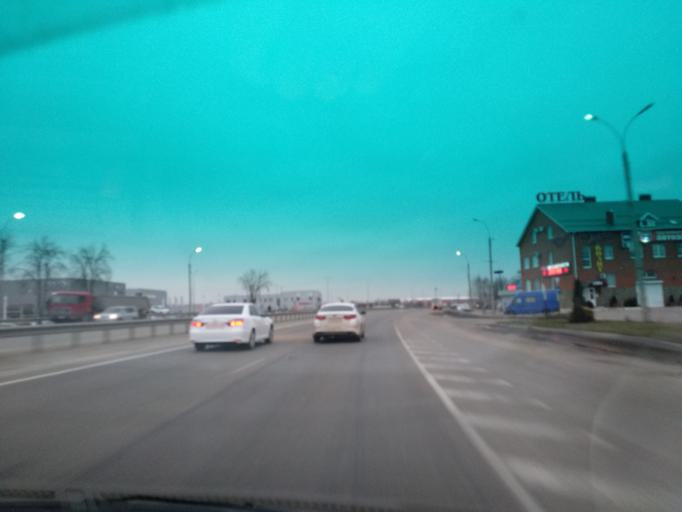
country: RU
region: Krasnodarskiy
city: Pashkovskiy
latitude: 45.0296
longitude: 39.1300
